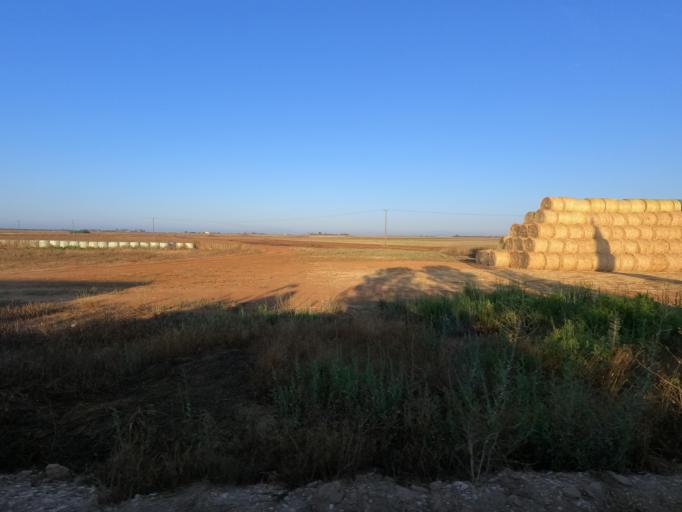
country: CY
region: Ammochostos
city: Achna
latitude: 35.0162
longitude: 33.8009
